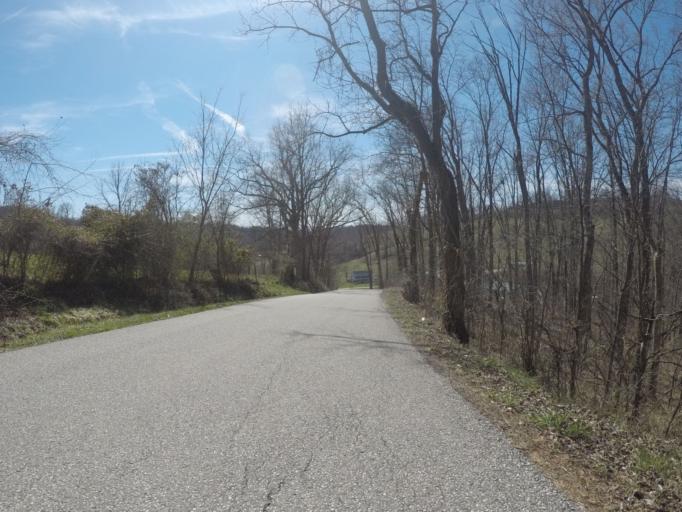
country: US
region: Ohio
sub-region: Lawrence County
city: South Point
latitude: 38.4798
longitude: -82.5657
